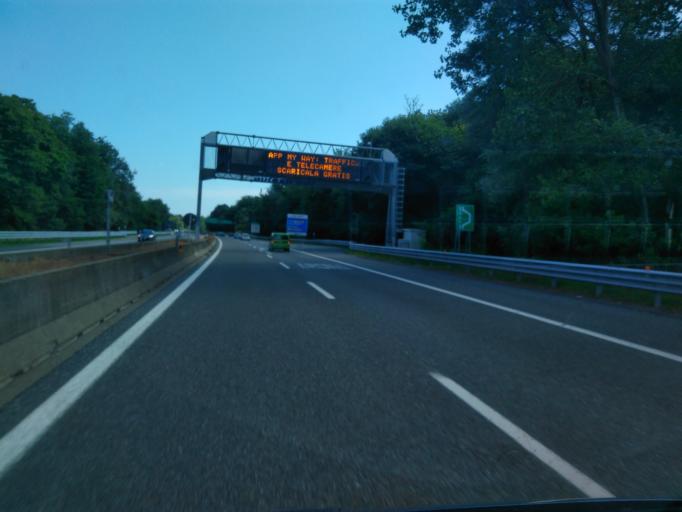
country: IT
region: Piedmont
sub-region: Provincia di Novara
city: Paruzzaro
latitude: 45.7377
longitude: 8.5046
